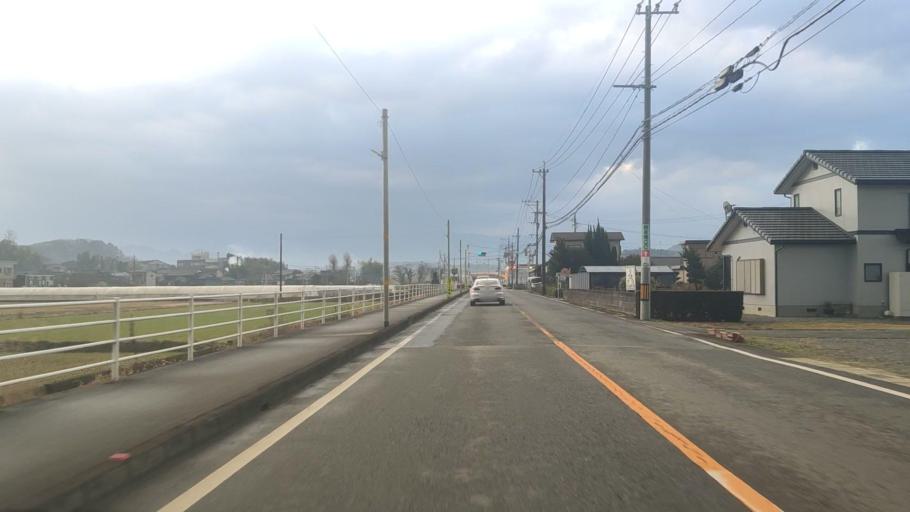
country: JP
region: Kumamoto
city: Uto
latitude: 32.7056
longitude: 130.7775
